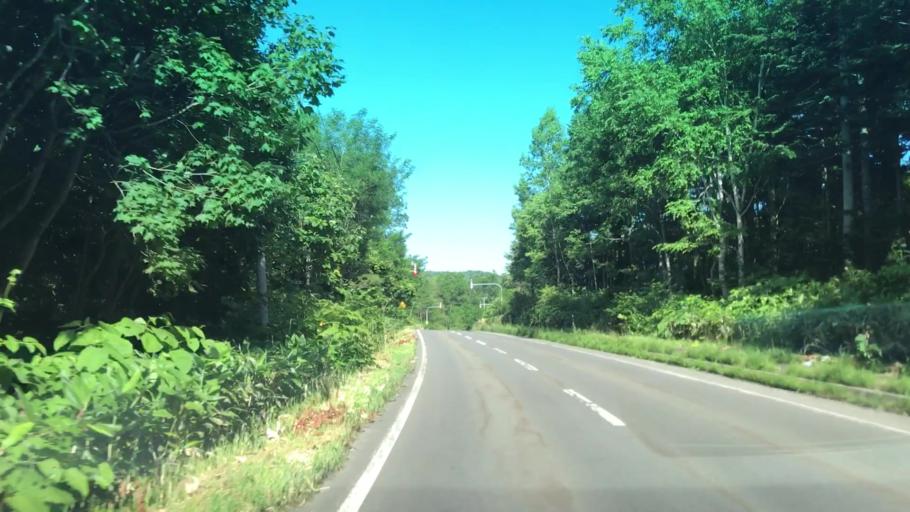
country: JP
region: Hokkaido
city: Yoichi
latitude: 43.0644
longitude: 140.7093
